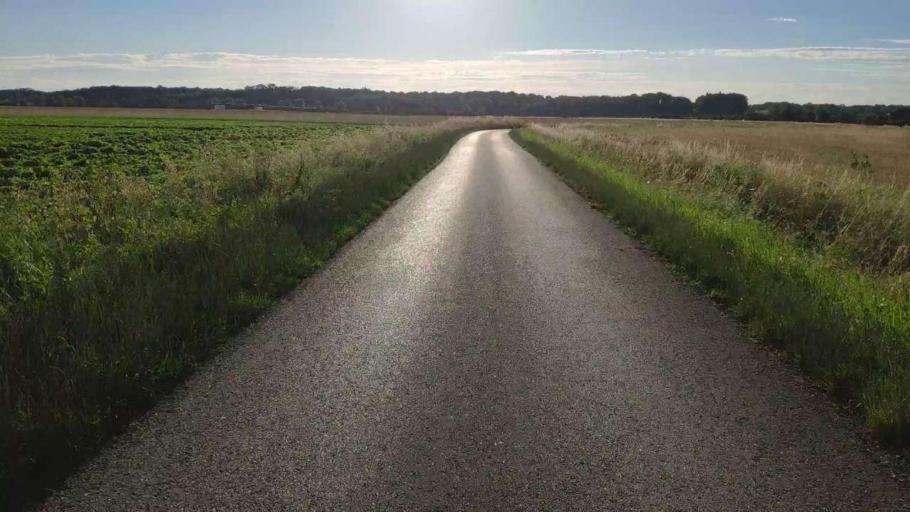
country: FR
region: Franche-Comte
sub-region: Departement du Jura
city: Bletterans
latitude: 46.7729
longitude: 5.4974
